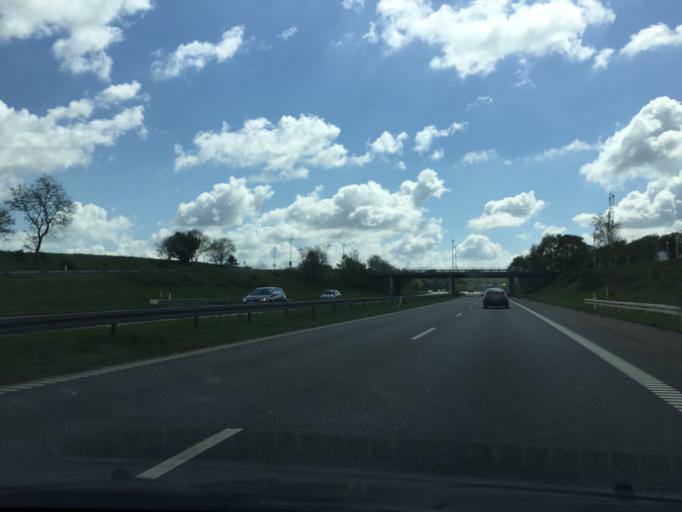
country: DK
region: Zealand
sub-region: Koge Kommune
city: Ejby
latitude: 55.4653
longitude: 12.1224
